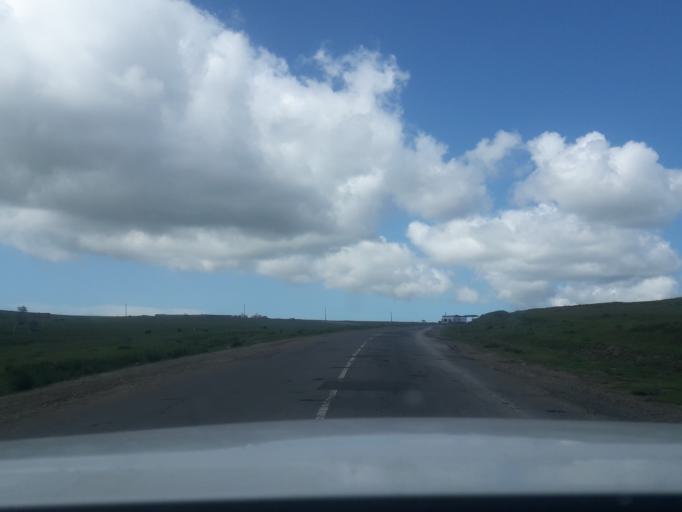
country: MN
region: Central Aimak
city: Ihsueuej
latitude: 48.1306
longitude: 106.4284
